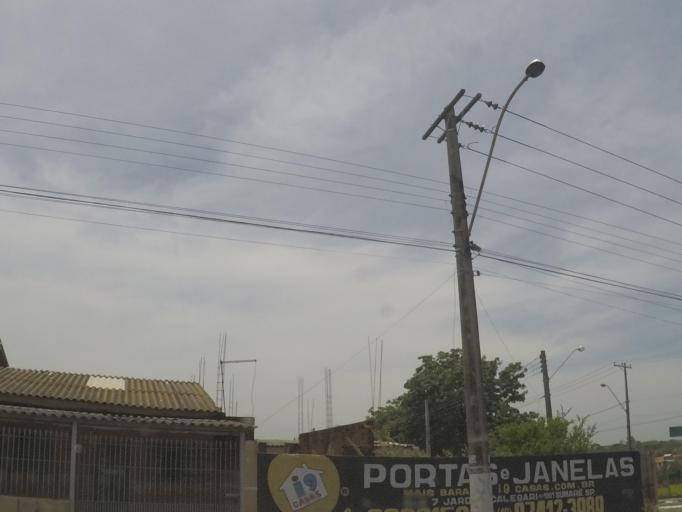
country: BR
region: Sao Paulo
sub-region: Hortolandia
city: Hortolandia
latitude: -22.8490
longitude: -47.1874
